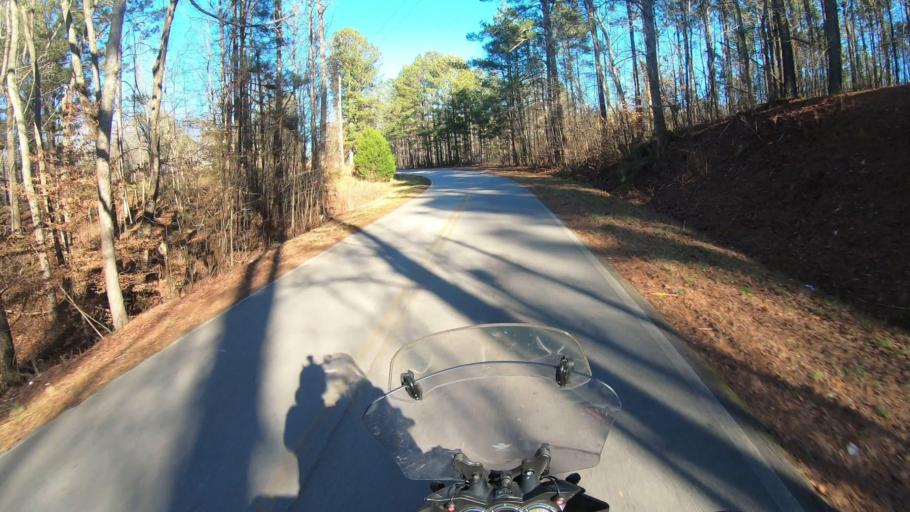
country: US
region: Georgia
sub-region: Haralson County
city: Tallapoosa
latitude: 33.8812
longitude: -85.3175
